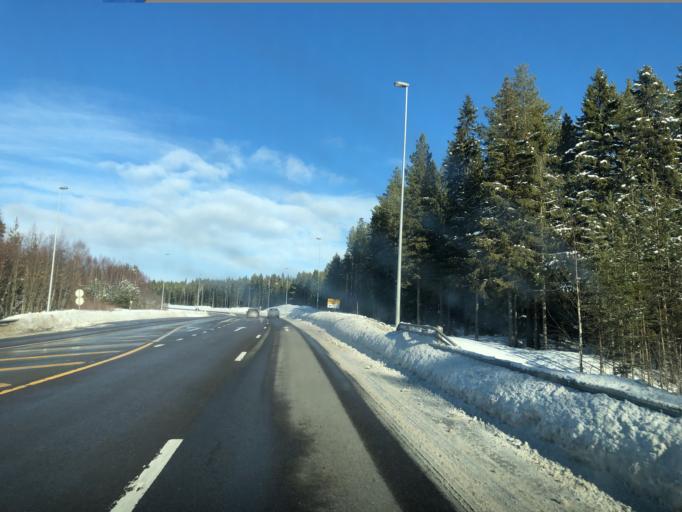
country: NO
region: Oppland
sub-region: Gran
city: Jaren
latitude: 60.4261
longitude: 10.5758
